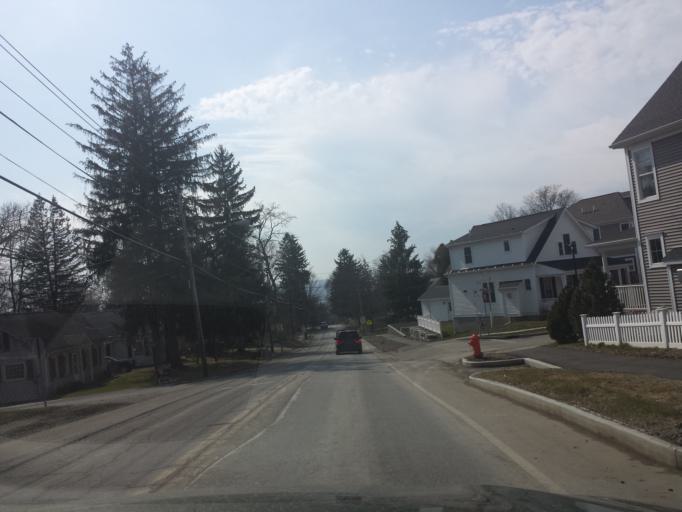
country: US
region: New York
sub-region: Tompkins County
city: East Ithaca
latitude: 42.4377
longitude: -76.4732
